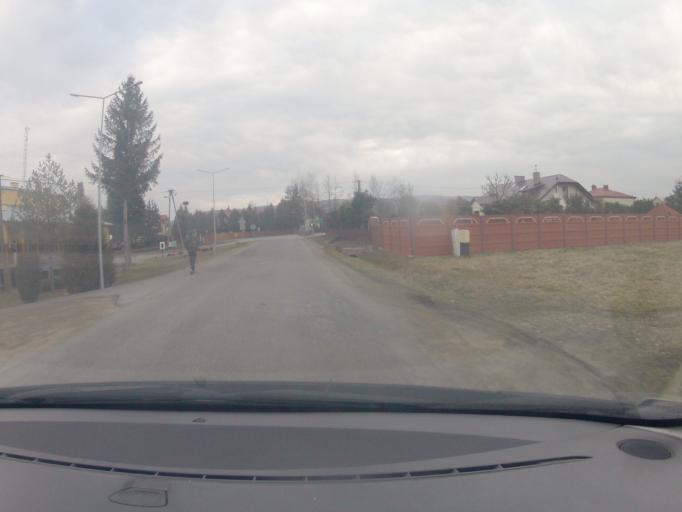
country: PL
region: Subcarpathian Voivodeship
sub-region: Powiat krosnienski
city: Dukla
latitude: 49.5577
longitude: 21.6269
